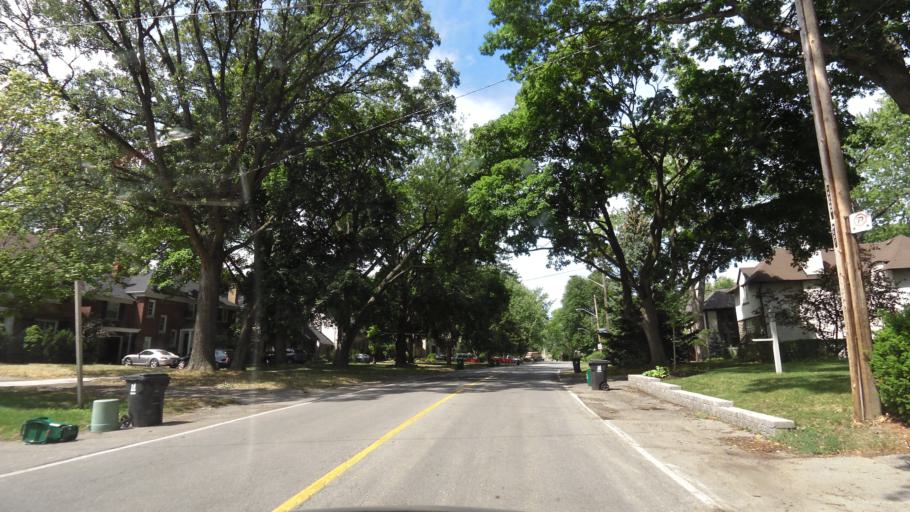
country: CA
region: Ontario
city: Etobicoke
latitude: 43.6544
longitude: -79.5129
